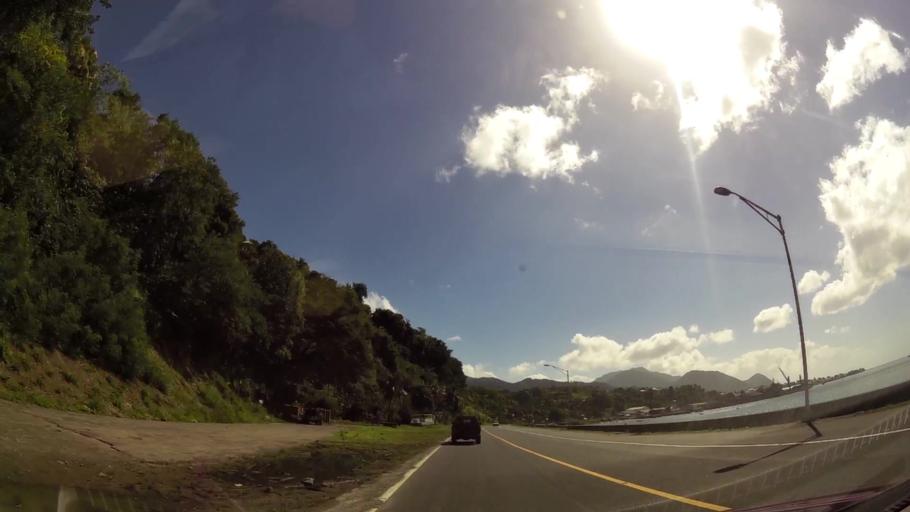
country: DM
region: Saint George
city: Roseau
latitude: 15.3180
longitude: -61.3911
